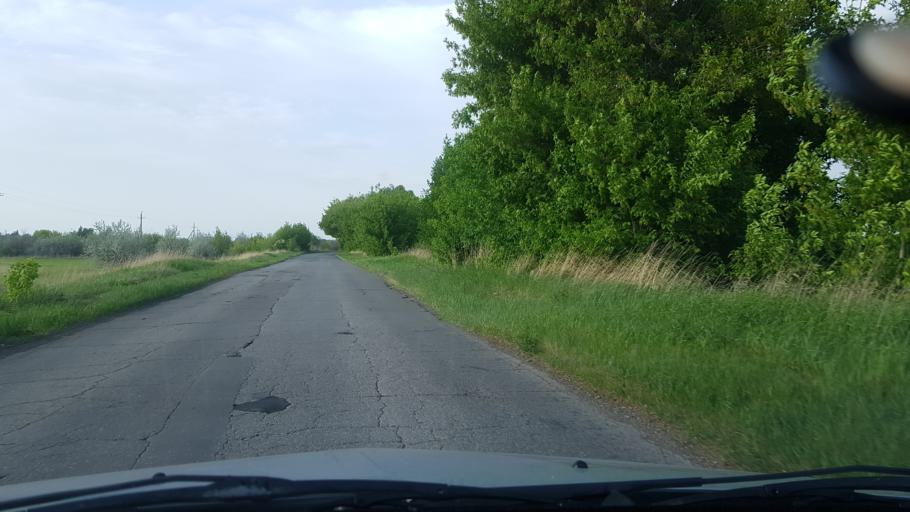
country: RU
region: Samara
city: Khryashchevka
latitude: 53.8241
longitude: 49.1221
